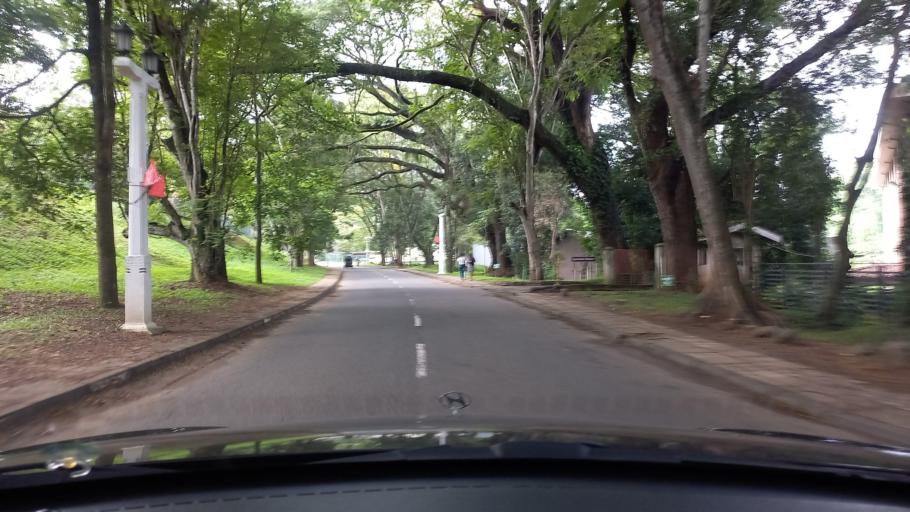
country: LK
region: Central
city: Kandy
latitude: 7.2648
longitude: 80.5969
